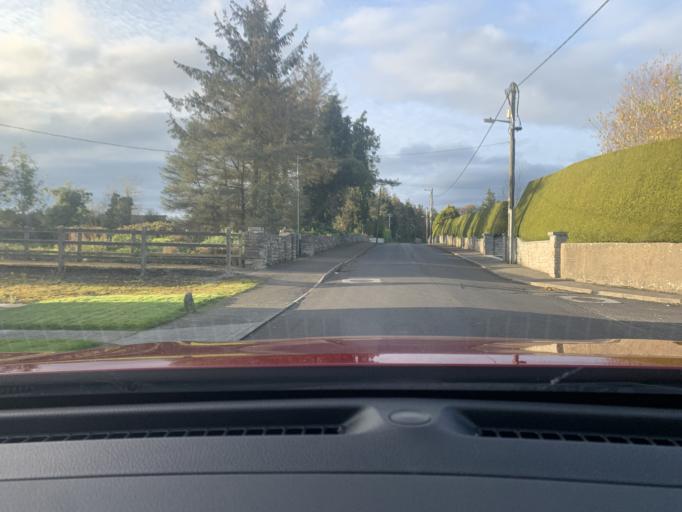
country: IE
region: Connaught
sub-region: Roscommon
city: Ballaghaderreen
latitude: 53.9046
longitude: -8.5764
